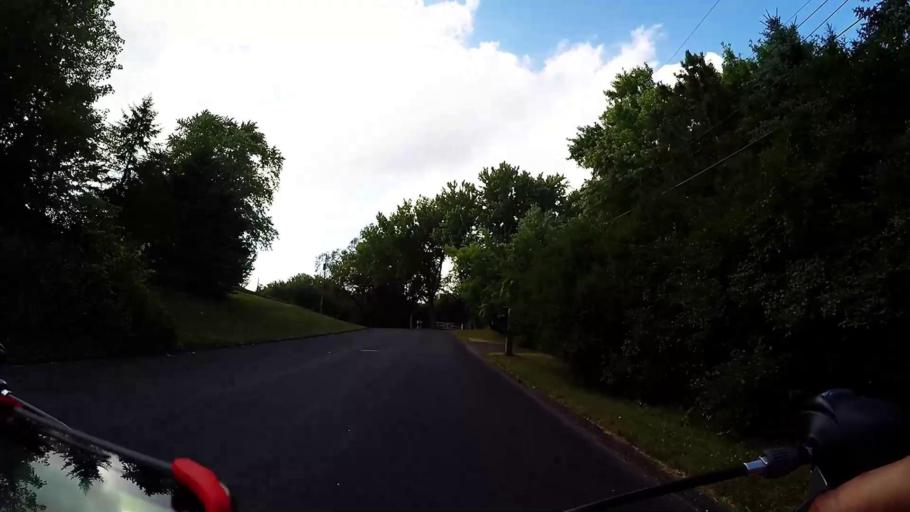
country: US
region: Minnesota
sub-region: Hennepin County
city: Eden Prairie
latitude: 44.8854
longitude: -93.4724
